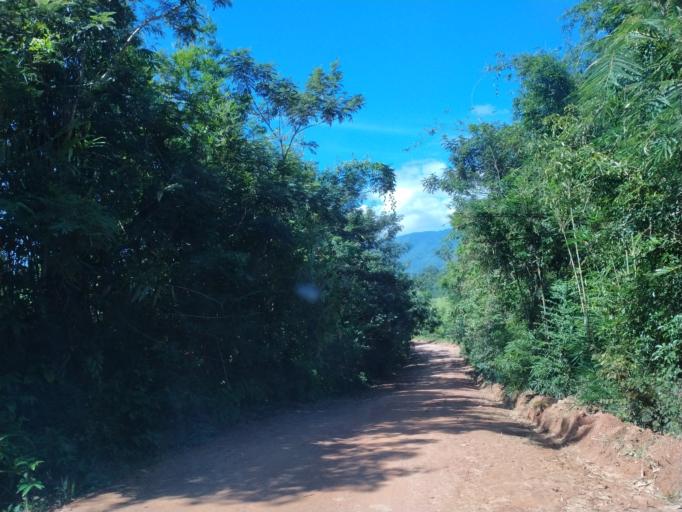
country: LA
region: Vientiane
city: Muang Phon-Hong
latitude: 18.6217
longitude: 102.8734
